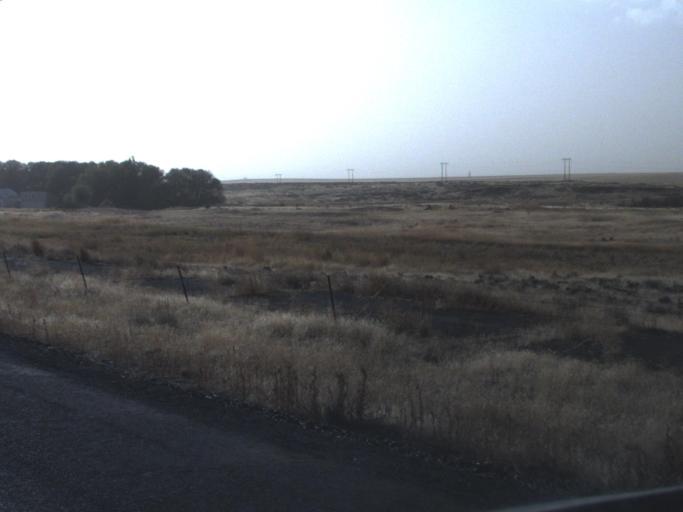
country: US
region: Washington
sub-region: Lincoln County
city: Davenport
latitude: 47.5146
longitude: -118.2182
